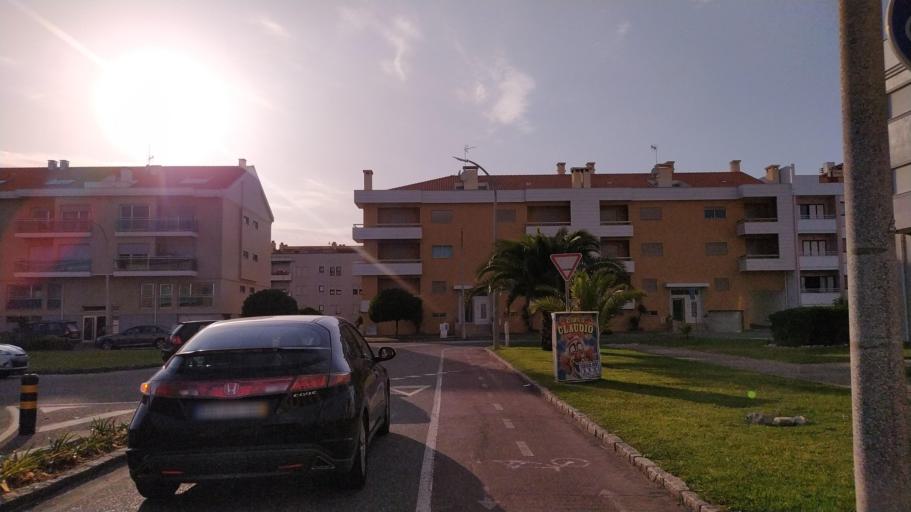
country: PT
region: Aveiro
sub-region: Ilhavo
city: Gafanha da Encarnacao
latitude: 40.5620
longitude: -8.7614
